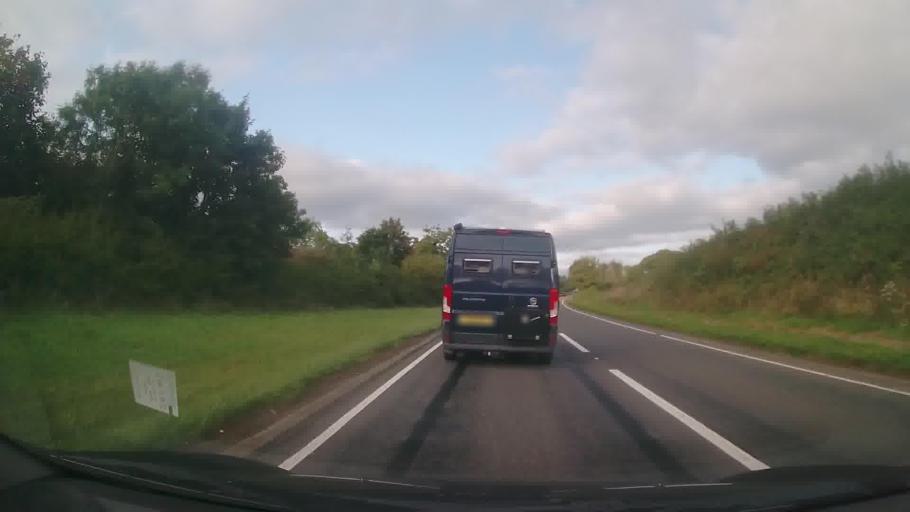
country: GB
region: Wales
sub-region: Pembrokeshire
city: Jeffreyston
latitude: 51.7141
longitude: -4.7614
